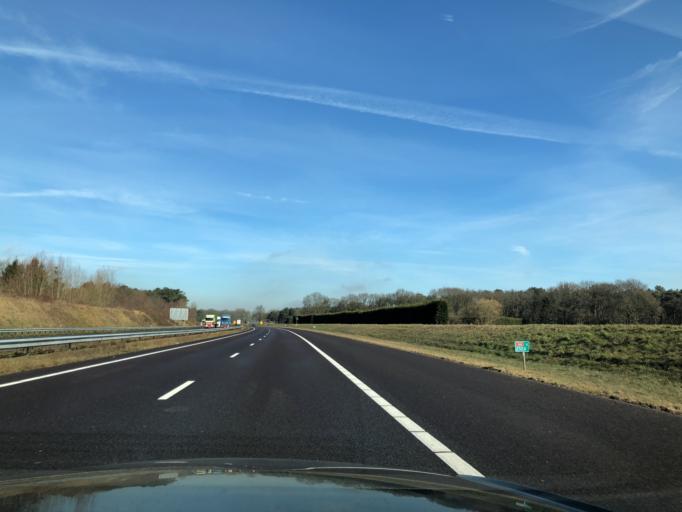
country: NL
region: North Brabant
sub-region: Gemeente Bergen op Zoom
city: Bergen op Zoom
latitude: 51.5160
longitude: 4.3104
